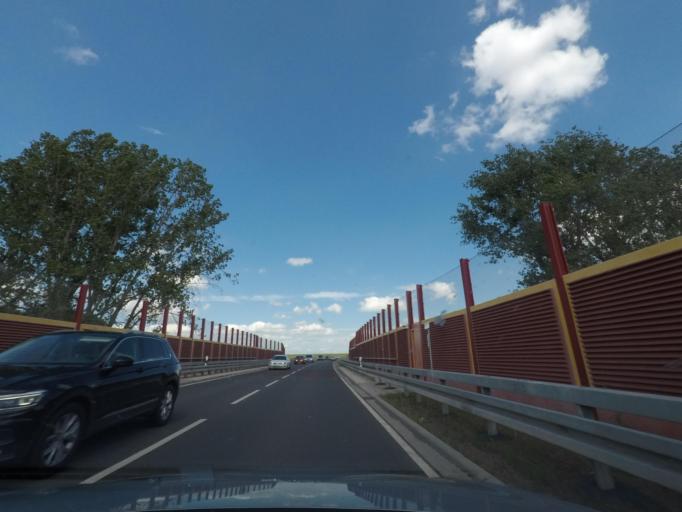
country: DE
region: Saxony-Anhalt
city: Harsleben
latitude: 51.8794
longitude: 11.0906
